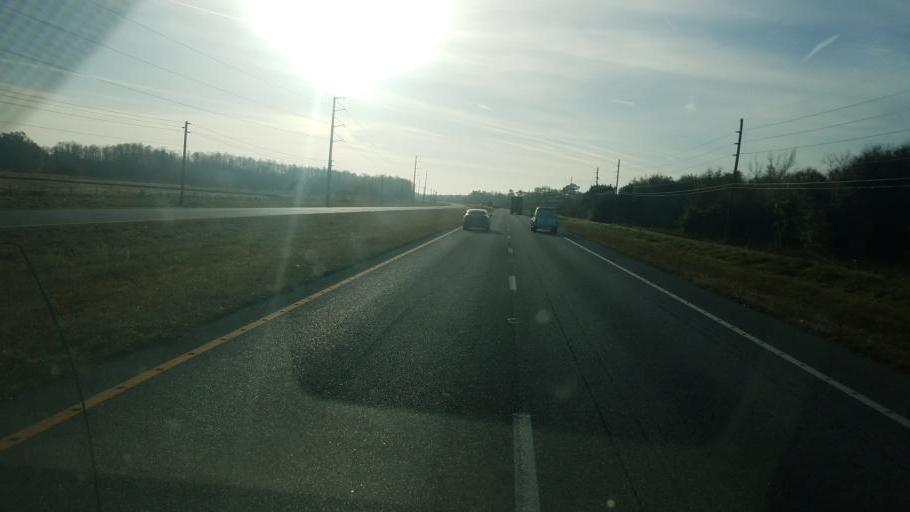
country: US
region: Florida
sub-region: Osceola County
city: Saint Cloud
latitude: 28.1544
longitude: -81.1083
